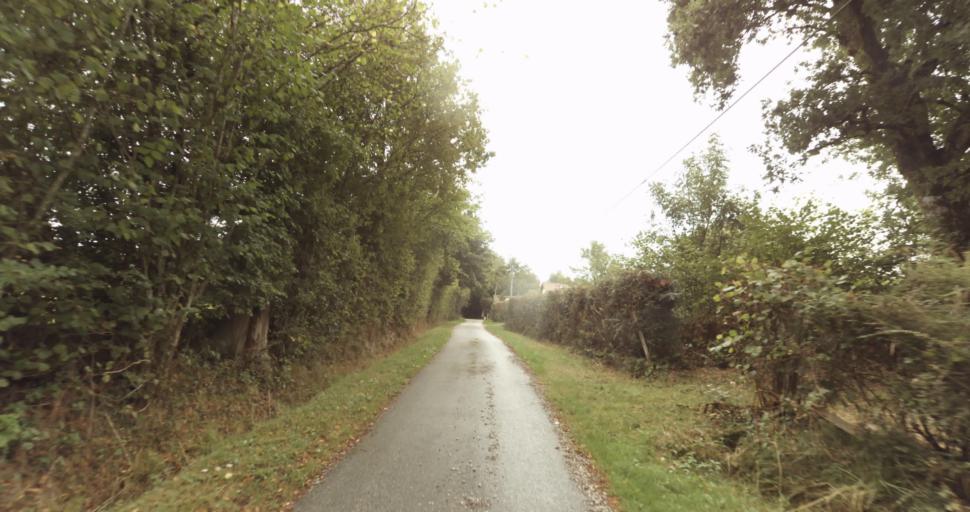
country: FR
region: Lower Normandy
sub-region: Departement de l'Orne
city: Sainte-Gauburge-Sainte-Colombe
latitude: 48.7503
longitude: 0.4249
